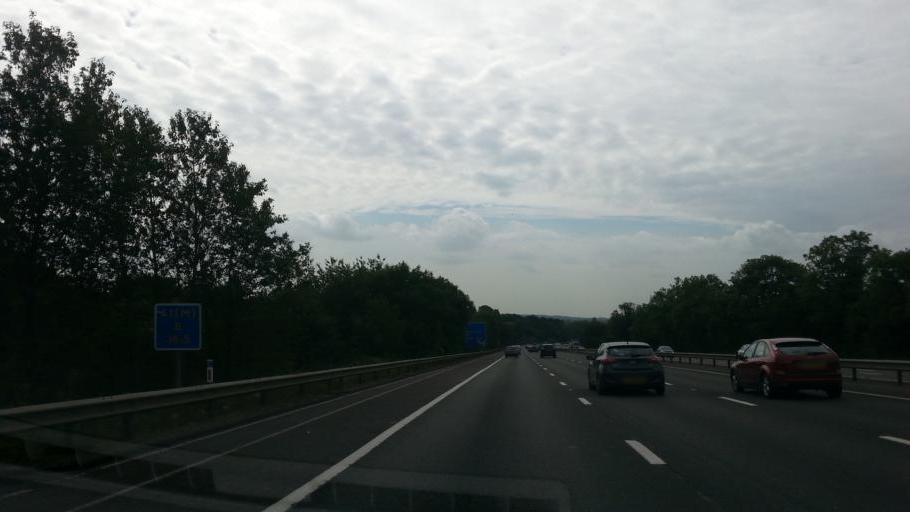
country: GB
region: England
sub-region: Hertfordshire
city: Welwyn Garden City
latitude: 51.7993
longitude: -0.2269
